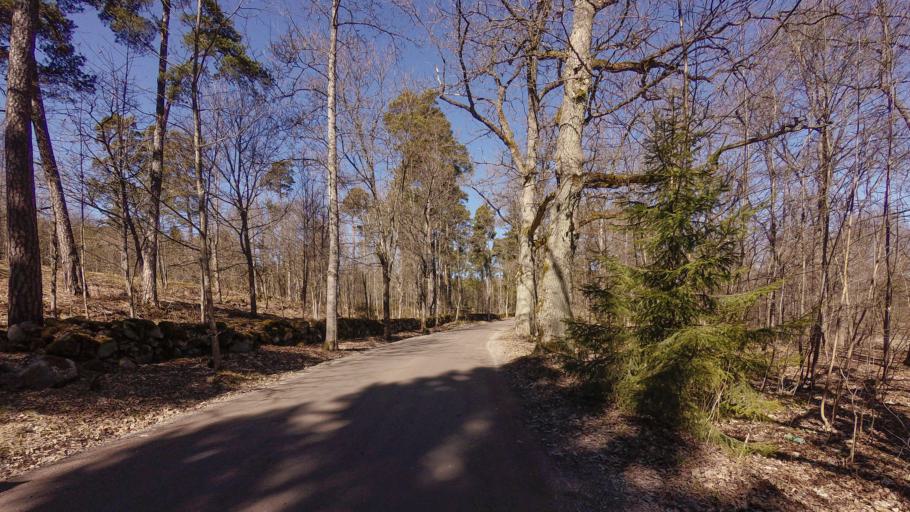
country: FI
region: Uusimaa
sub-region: Helsinki
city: Helsinki
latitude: 60.1653
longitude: 25.0278
